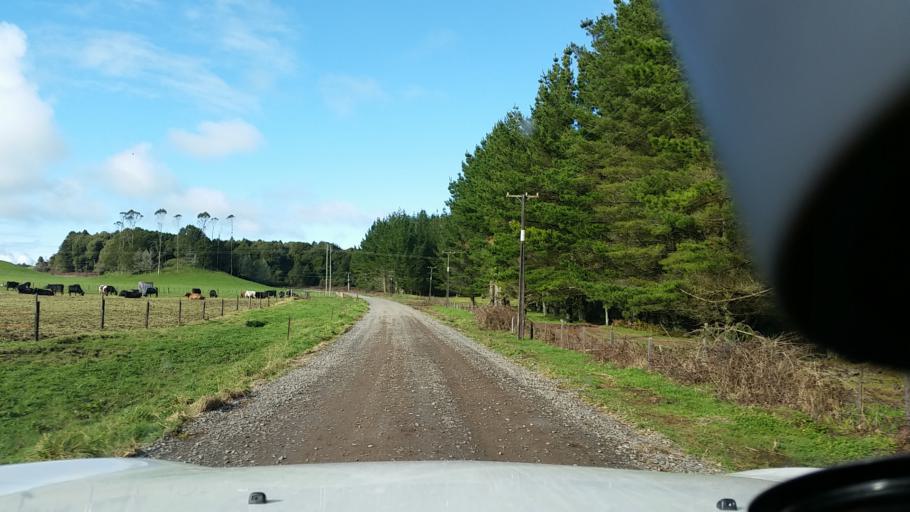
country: NZ
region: Bay of Plenty
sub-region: Rotorua District
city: Rotorua
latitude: -38.0814
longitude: 176.0421
